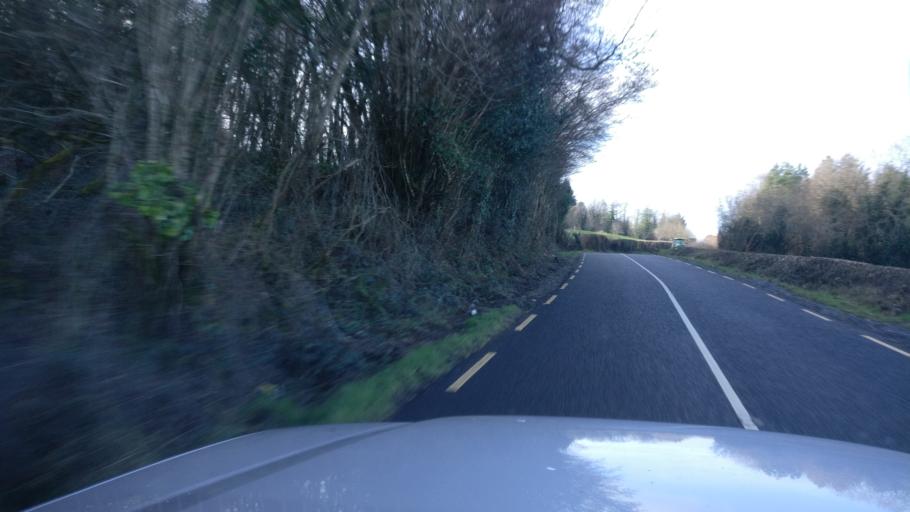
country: IE
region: Leinster
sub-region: Laois
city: Portlaoise
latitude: 53.0119
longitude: -7.2438
